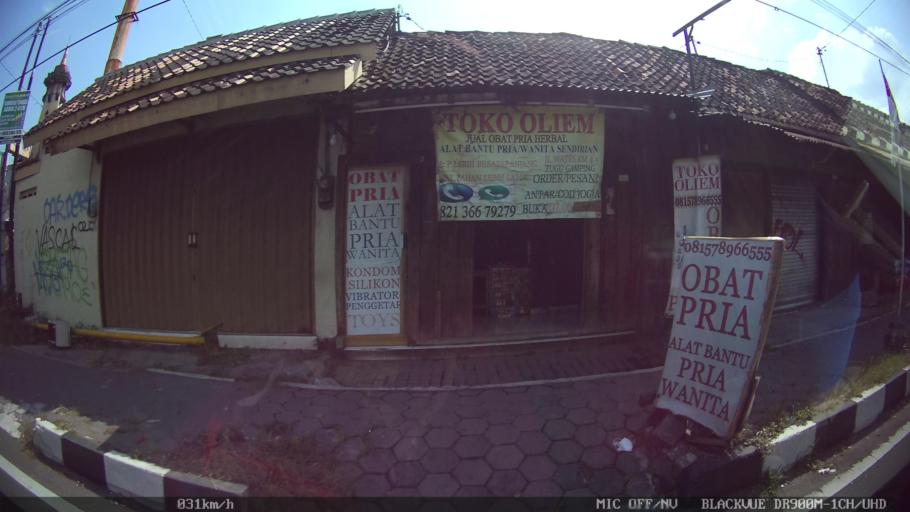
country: ID
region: Daerah Istimewa Yogyakarta
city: Gamping Lor
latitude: -7.8003
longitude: 110.3256
